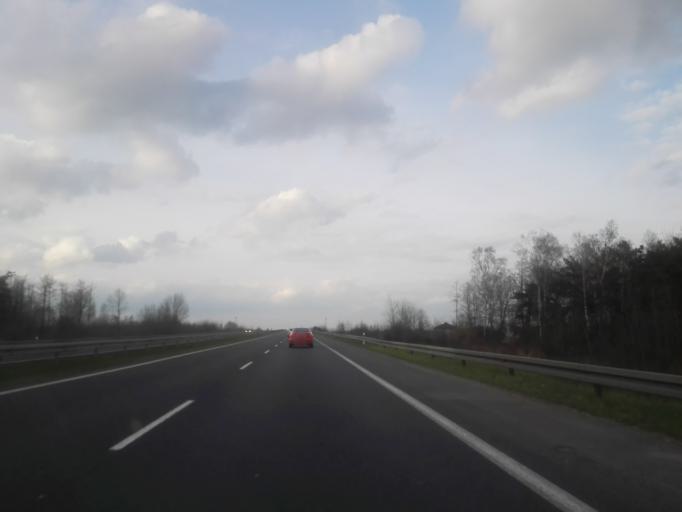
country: PL
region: Lodz Voivodeship
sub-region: Powiat piotrkowski
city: Wola Krzysztoporska
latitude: 51.3496
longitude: 19.6032
